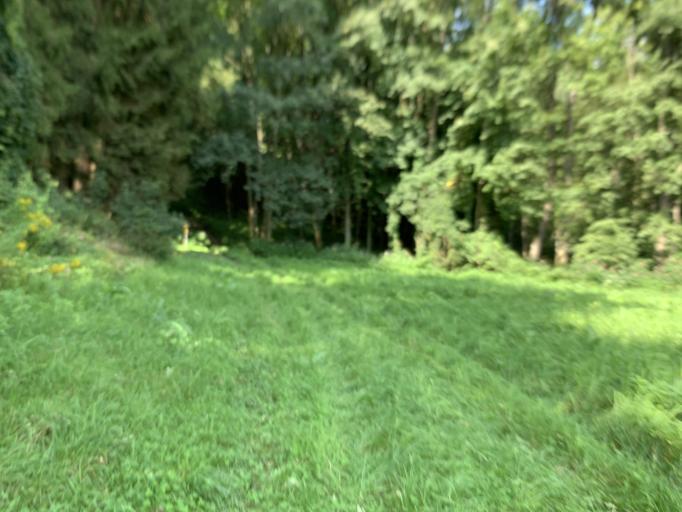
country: DE
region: Bavaria
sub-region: Upper Bavaria
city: Langenbach
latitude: 48.4136
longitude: 11.8387
